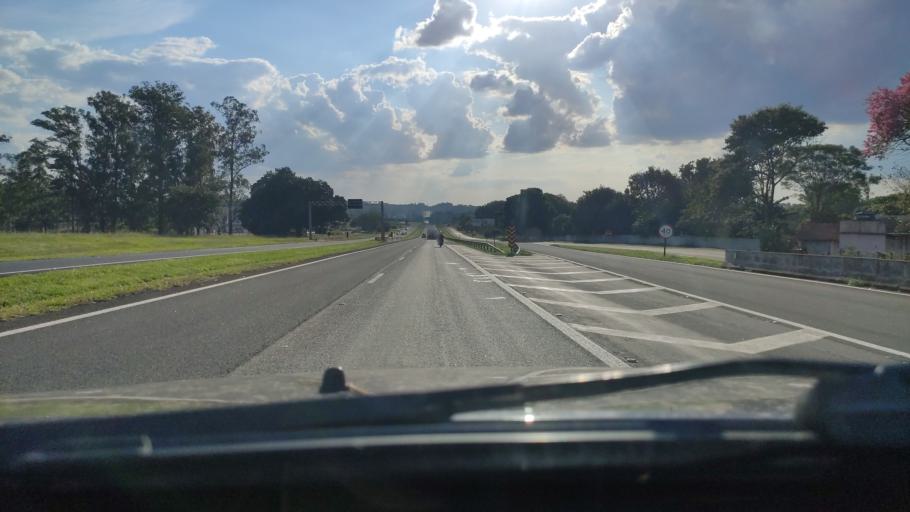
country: BR
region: Sao Paulo
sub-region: Mogi-Mirim
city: Mogi Mirim
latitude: -22.4554
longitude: -46.9193
